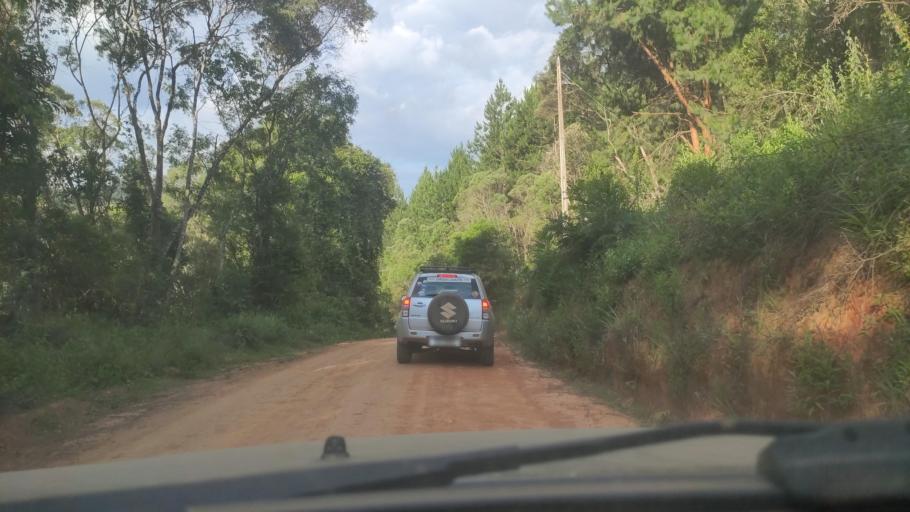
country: BR
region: Minas Gerais
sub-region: Cambui
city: Cambui
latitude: -22.7608
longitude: -45.9575
